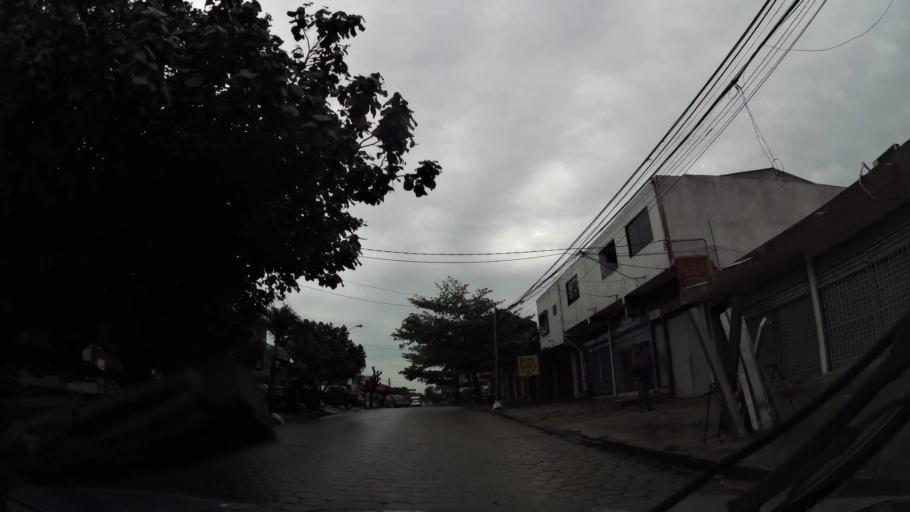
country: BO
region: Santa Cruz
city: Santa Cruz de la Sierra
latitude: -17.8047
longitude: -63.1903
